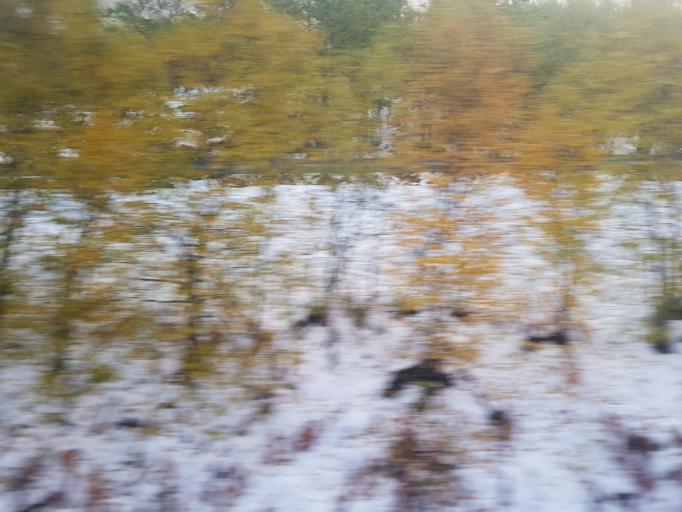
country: NO
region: Sor-Trondelag
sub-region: Oppdal
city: Oppdal
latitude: 62.4966
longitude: 9.5929
